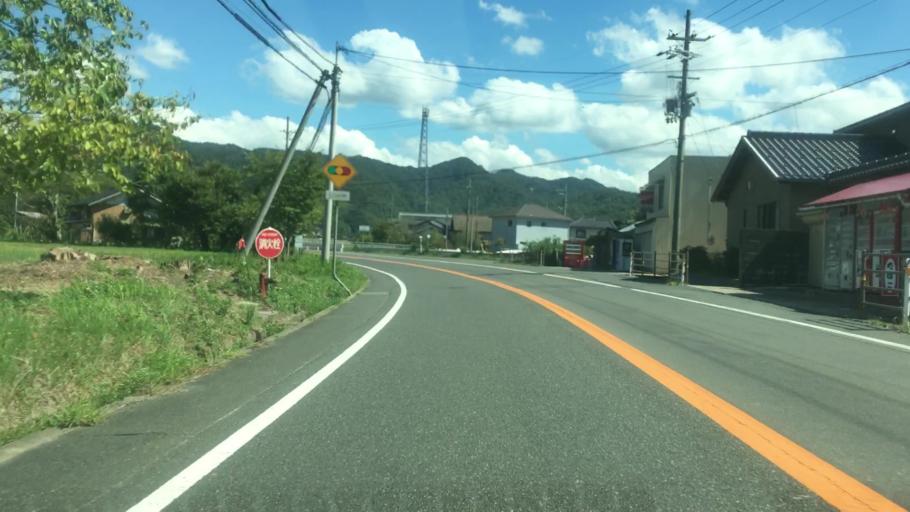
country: JP
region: Hyogo
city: Toyooka
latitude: 35.5794
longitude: 134.9708
